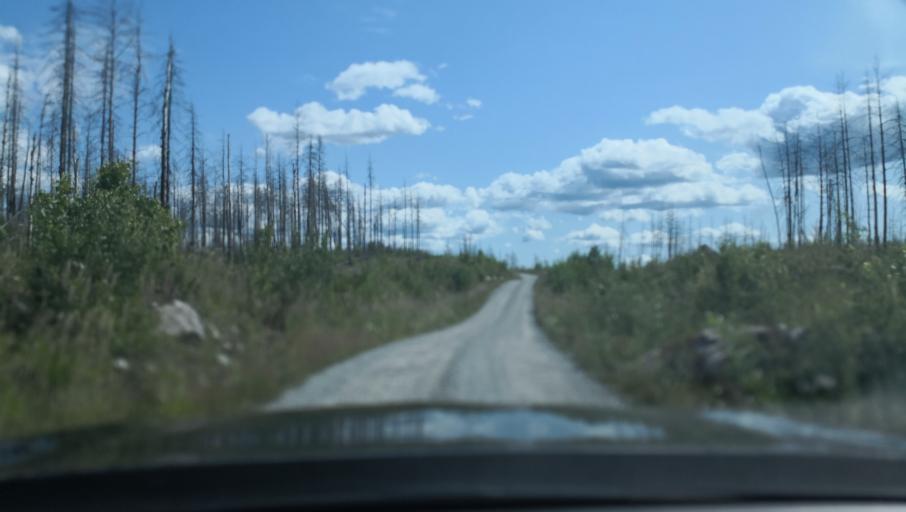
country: SE
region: Vaestmanland
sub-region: Surahammars Kommun
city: Ramnas
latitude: 59.8993
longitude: 16.1100
